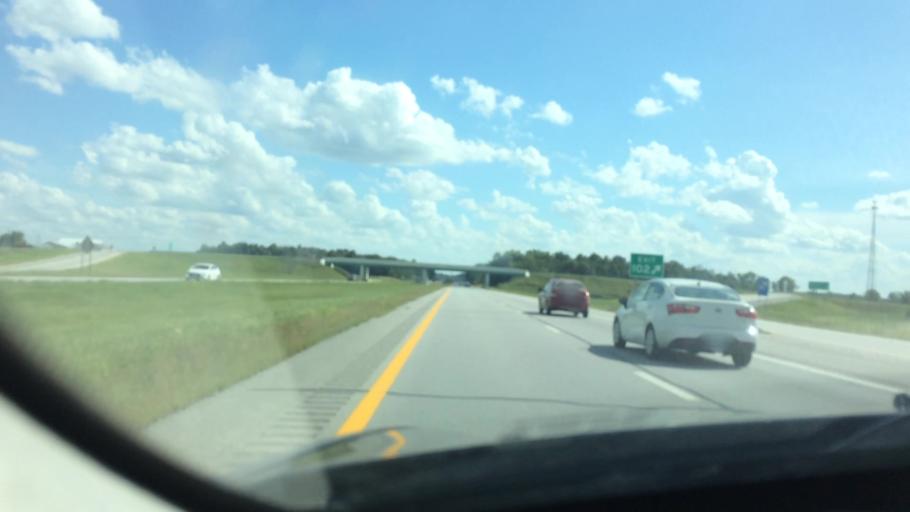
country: US
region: Ohio
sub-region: Shelby County
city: Botkins
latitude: 40.4420
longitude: -84.1694
